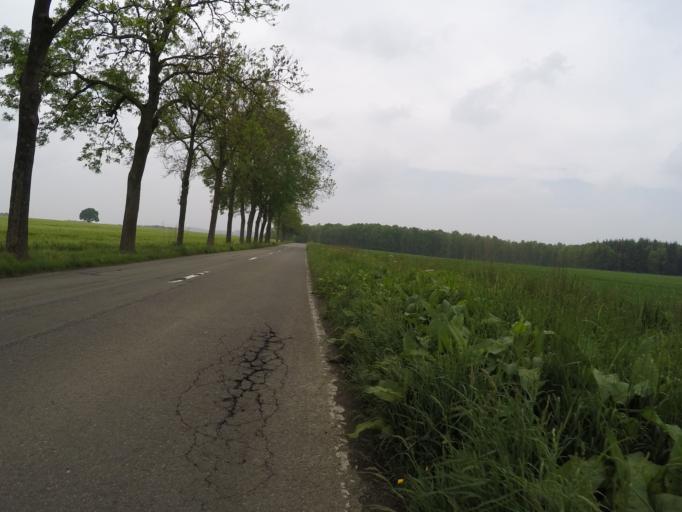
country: BE
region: Wallonia
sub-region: Province de Namur
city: Assesse
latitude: 50.3129
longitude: 5.0425
